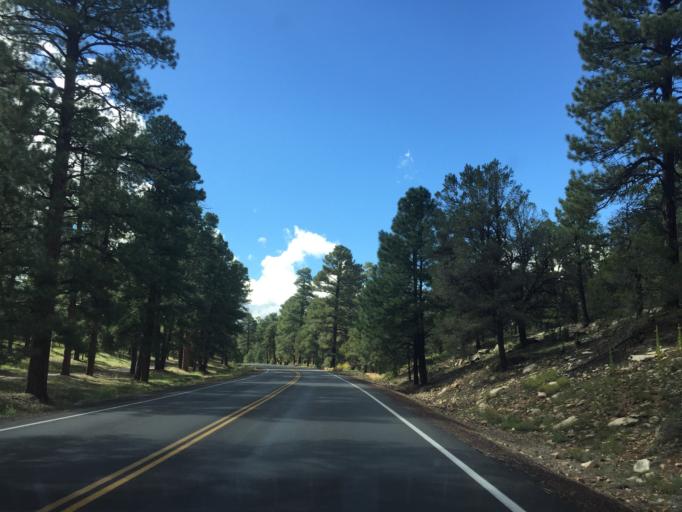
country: US
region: Arizona
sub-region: Coconino County
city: Grand Canyon
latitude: 36.0555
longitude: -112.1288
